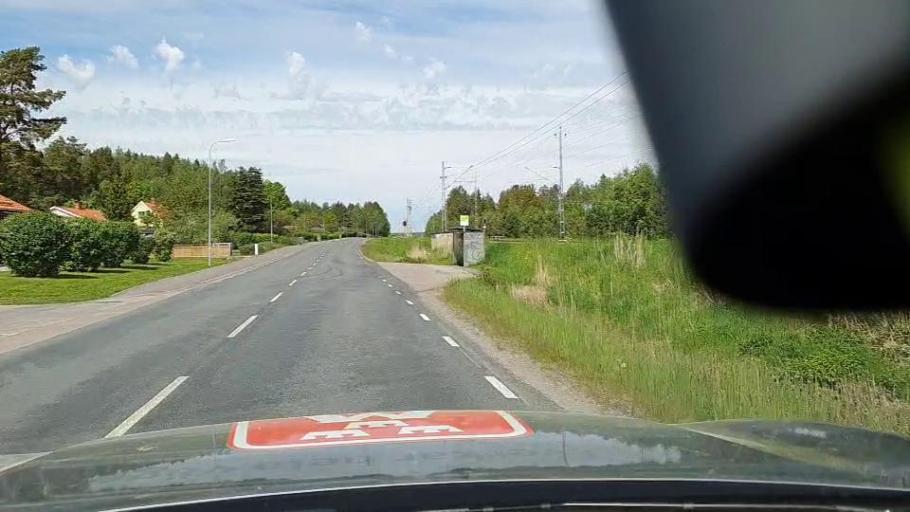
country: SE
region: Soedermanland
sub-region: Eskilstuna Kommun
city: Skogstorp
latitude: 59.2969
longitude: 16.4586
